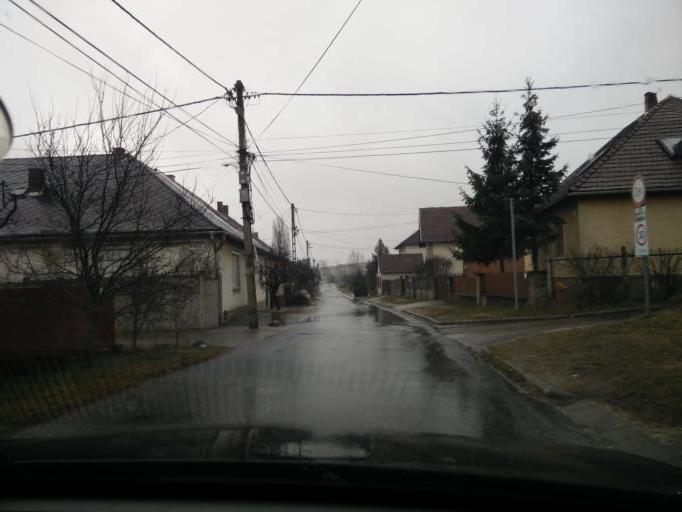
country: HU
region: Pest
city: Pilisszentivan
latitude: 47.6119
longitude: 18.8981
